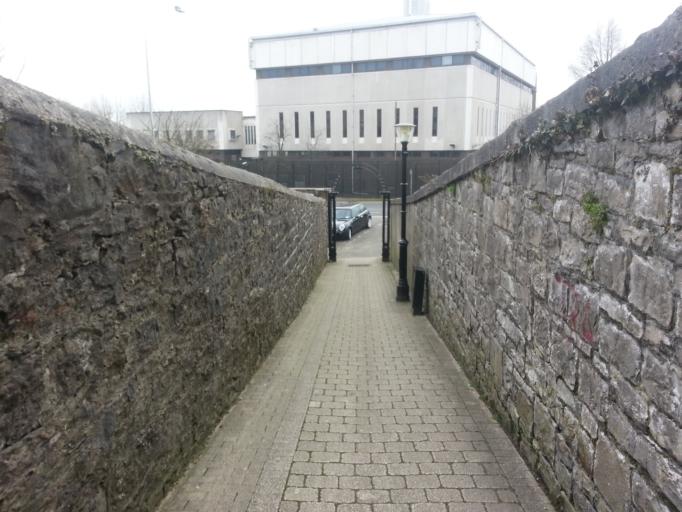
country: GB
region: Northern Ireland
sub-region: Fermanagh District
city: Enniskillen
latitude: 54.3459
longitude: -7.6415
